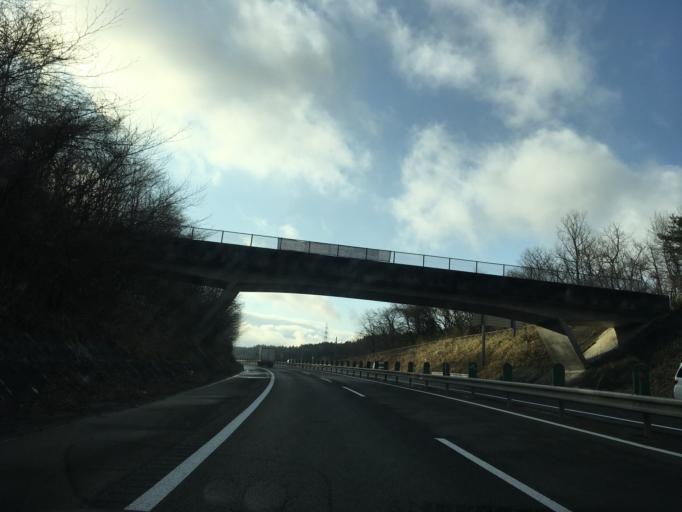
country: JP
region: Miyagi
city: Okawara
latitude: 38.1550
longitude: 140.6948
